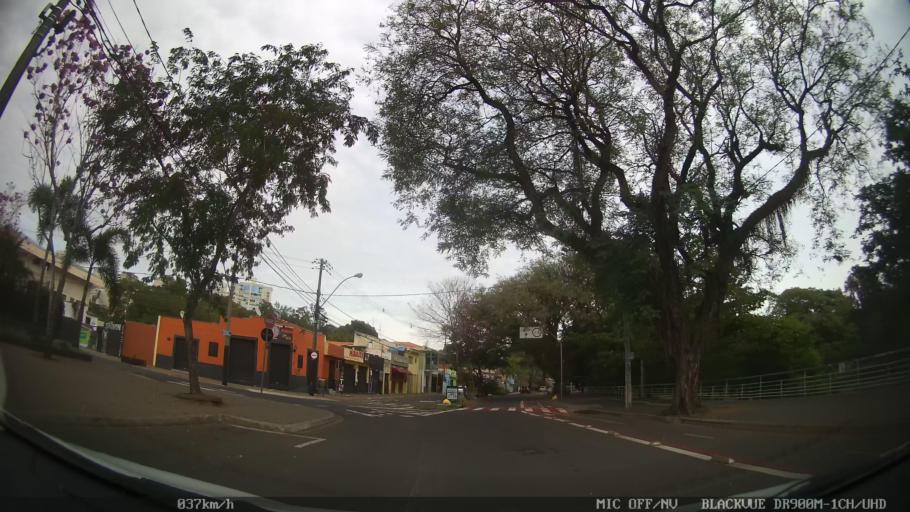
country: BR
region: Sao Paulo
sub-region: Piracicaba
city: Piracicaba
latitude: -22.7240
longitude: -47.6569
